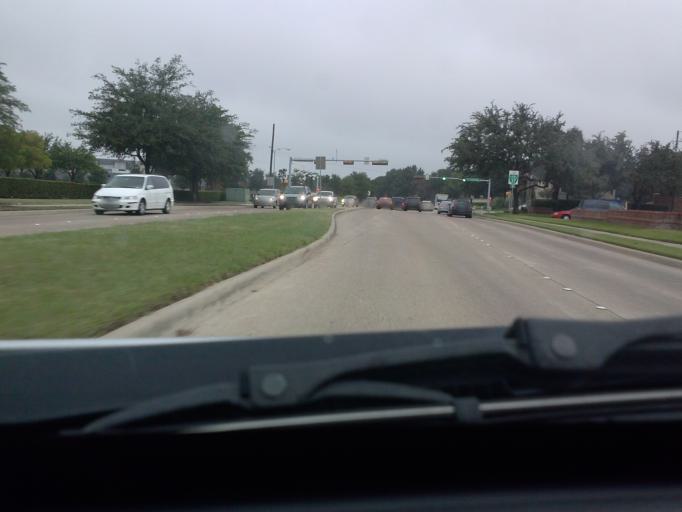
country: US
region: Texas
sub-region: Collin County
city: Plano
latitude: 33.0555
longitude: -96.7893
